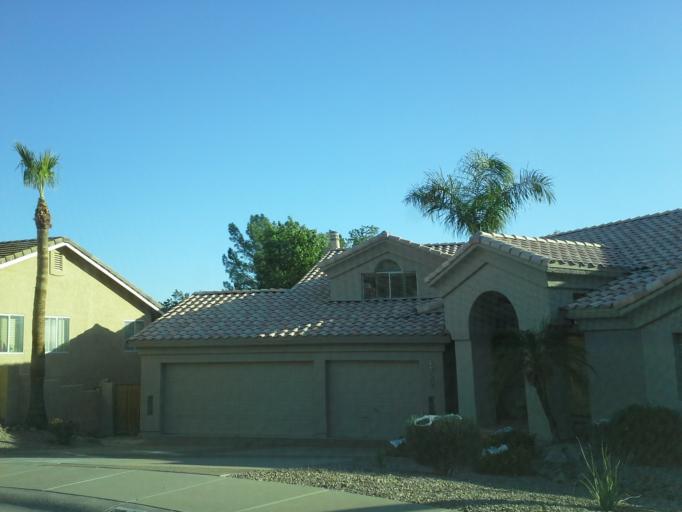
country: US
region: Arizona
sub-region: Maricopa County
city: Glendale
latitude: 33.6029
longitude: -112.0960
